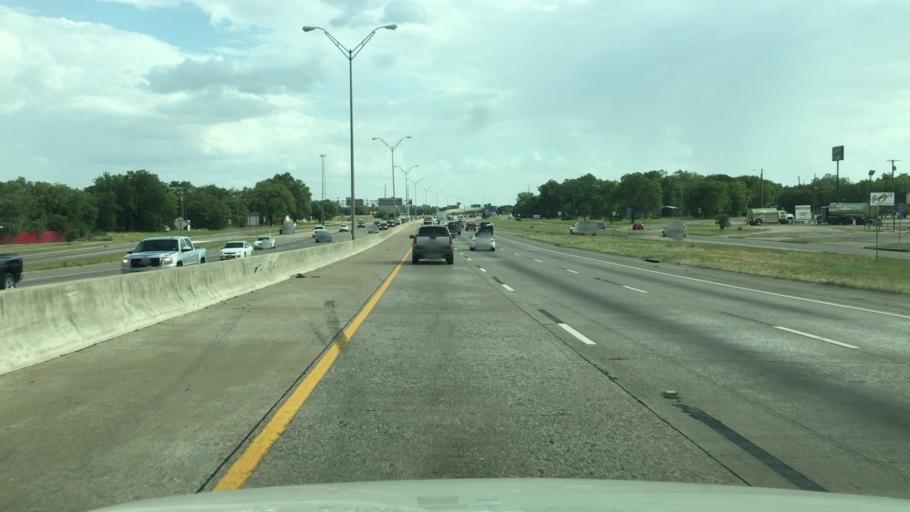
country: US
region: Texas
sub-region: McLennan County
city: Beverly
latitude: 31.5339
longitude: -97.1302
